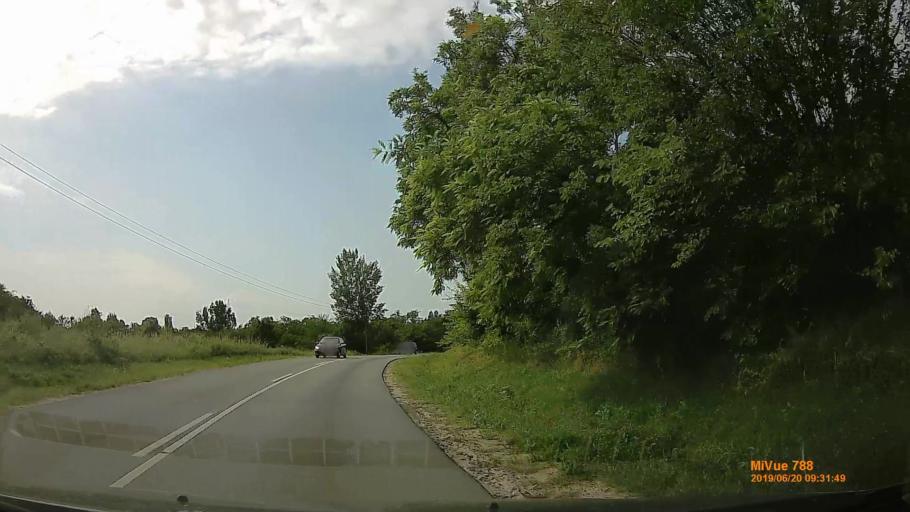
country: HU
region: Baranya
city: Pecsvarad
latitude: 46.1419
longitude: 18.4059
